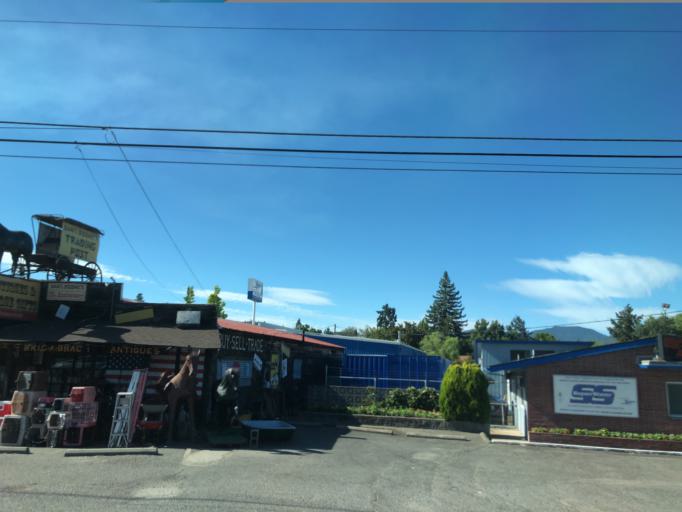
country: US
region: Oregon
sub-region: Josephine County
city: Grants Pass
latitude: 42.4243
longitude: -123.3363
